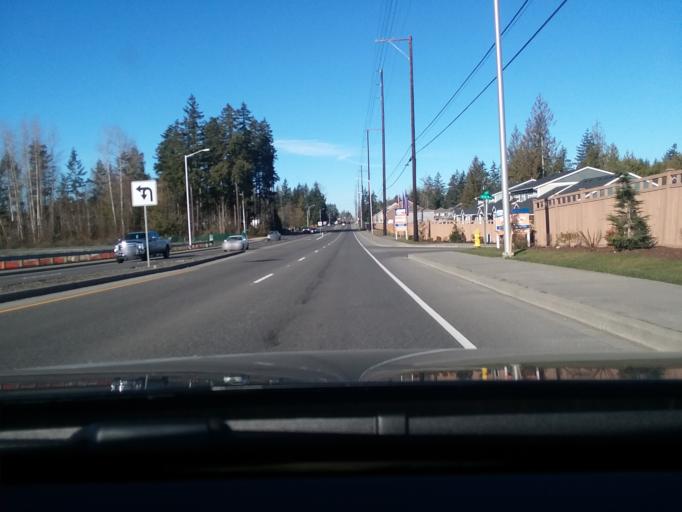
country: US
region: Washington
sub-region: Pierce County
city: Frederickson
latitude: 47.0966
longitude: -122.3177
